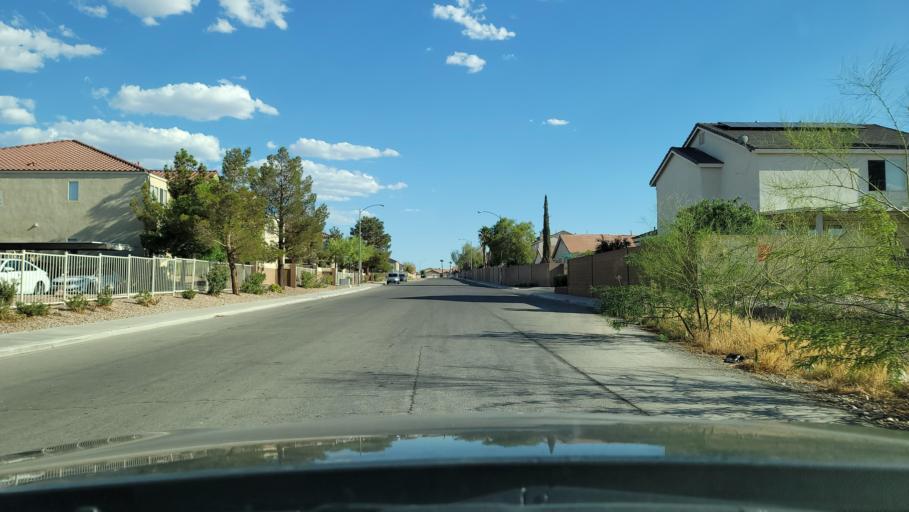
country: US
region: Nevada
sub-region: Clark County
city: Spring Valley
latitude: 36.0844
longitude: -115.2542
